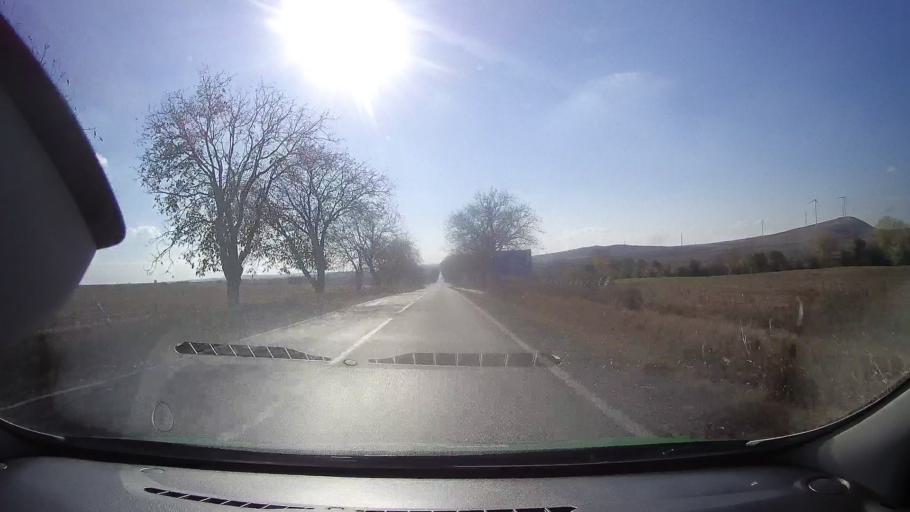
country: RO
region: Tulcea
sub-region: Comuna Ceamurlia de Jos
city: Ceamurlia de Jos
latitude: 44.7784
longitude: 28.6889
